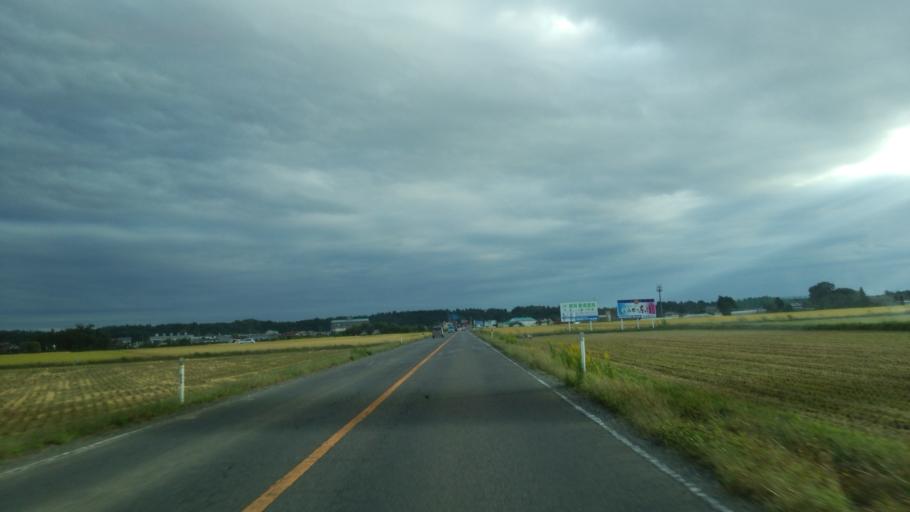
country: JP
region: Fukushima
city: Koriyama
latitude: 37.3703
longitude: 140.3407
